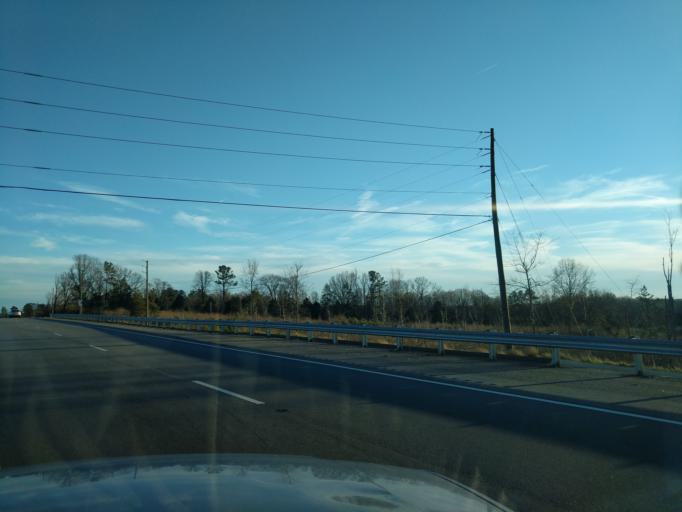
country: US
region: Georgia
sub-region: Franklin County
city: Lavonia
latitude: 34.4702
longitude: -83.1756
